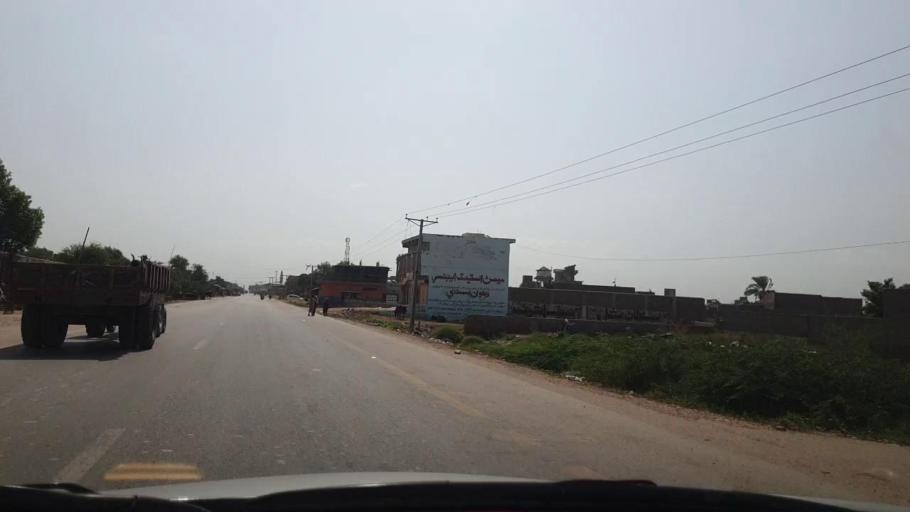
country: PK
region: Sindh
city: Matli
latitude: 25.0376
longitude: 68.6497
